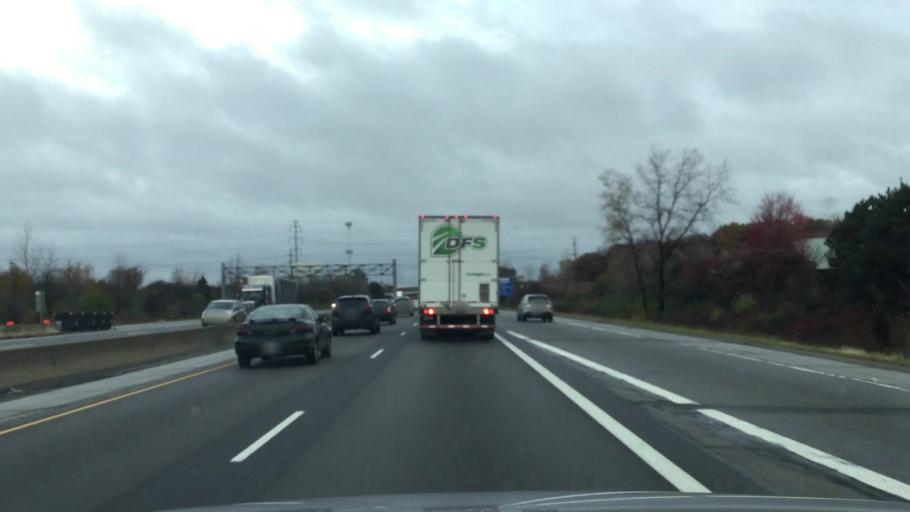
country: US
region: Michigan
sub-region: Washtenaw County
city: Ann Arbor
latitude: 42.2282
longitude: -83.6909
